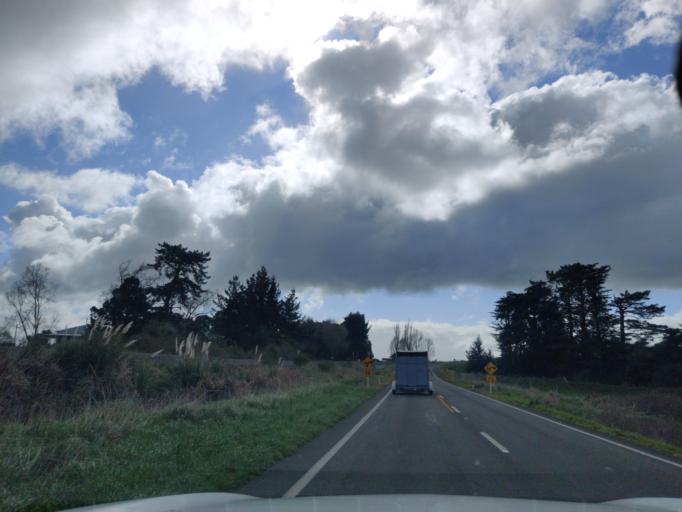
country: NZ
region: Manawatu-Wanganui
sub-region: Palmerston North City
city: Palmerston North
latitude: -40.4567
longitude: 175.5179
